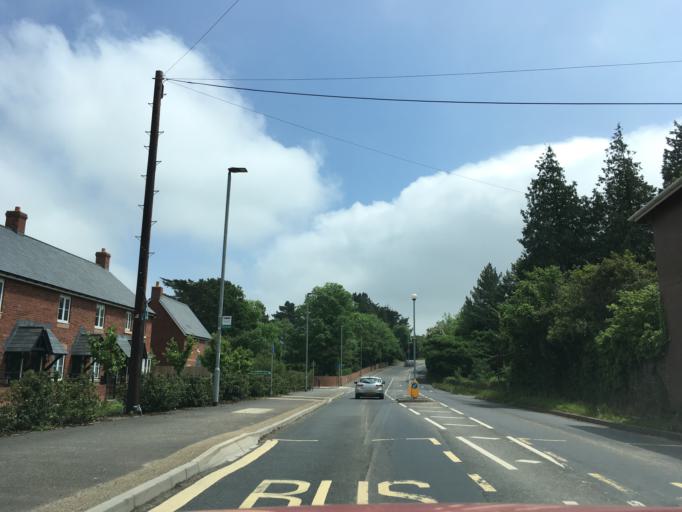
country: GB
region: England
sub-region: Devon
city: Totnes
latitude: 50.4403
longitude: -3.6969
